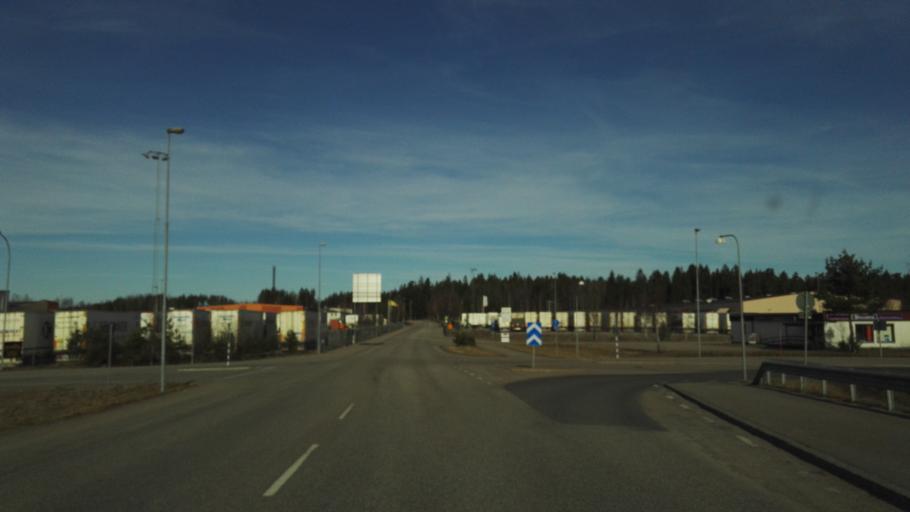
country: SE
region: Kronoberg
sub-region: Vaxjo Kommun
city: Vaexjoe
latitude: 56.9101
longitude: 14.8371
